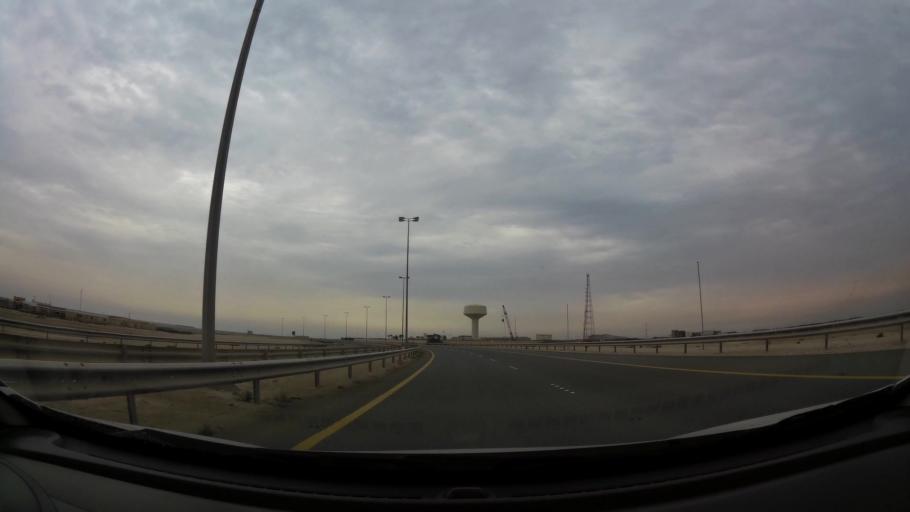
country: BH
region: Central Governorate
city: Dar Kulayb
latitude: 25.8422
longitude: 50.5845
